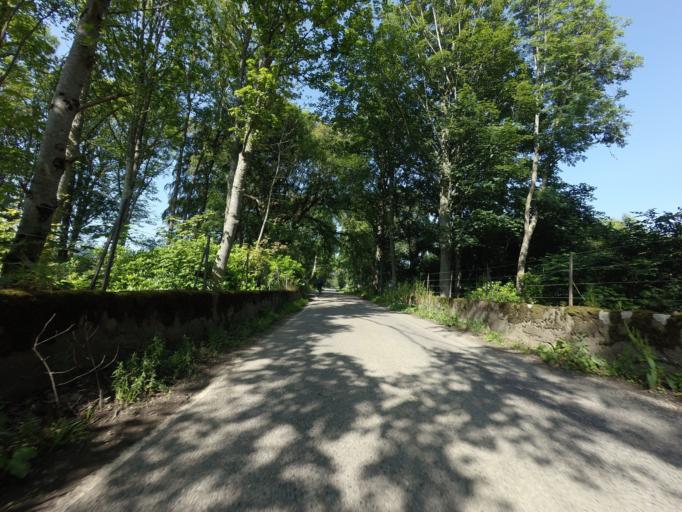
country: GB
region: Scotland
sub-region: Highland
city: Evanton
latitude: 57.6414
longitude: -4.3586
